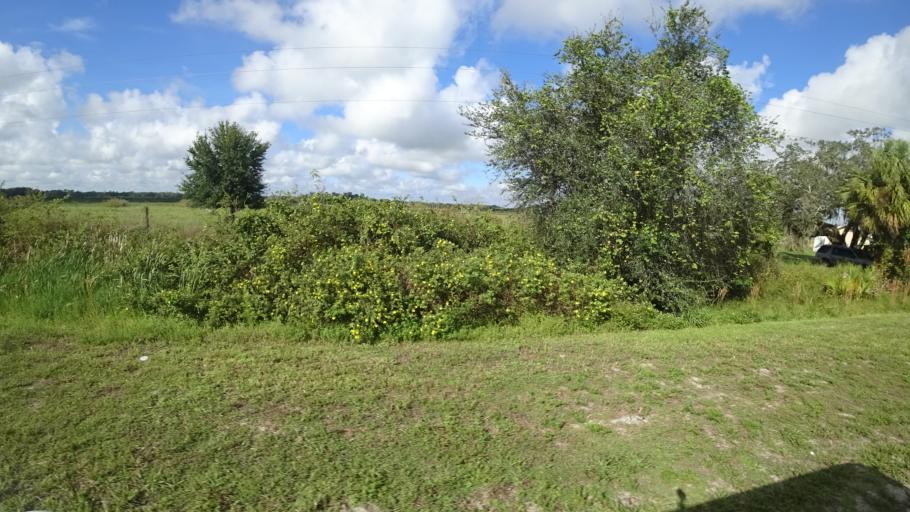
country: US
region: Florida
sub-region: Sarasota County
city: Lake Sarasota
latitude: 27.3480
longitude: -82.2439
